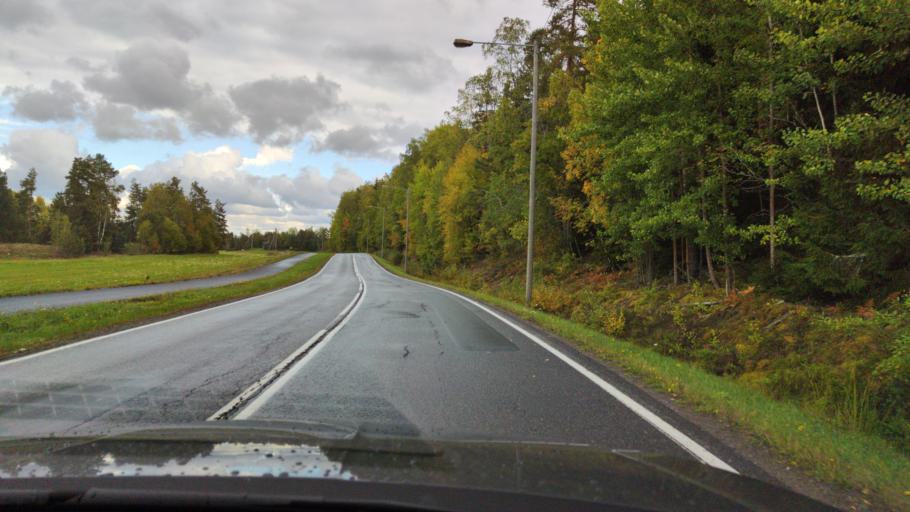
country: FI
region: Varsinais-Suomi
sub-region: Turku
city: Turku
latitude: 60.3620
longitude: 22.1917
